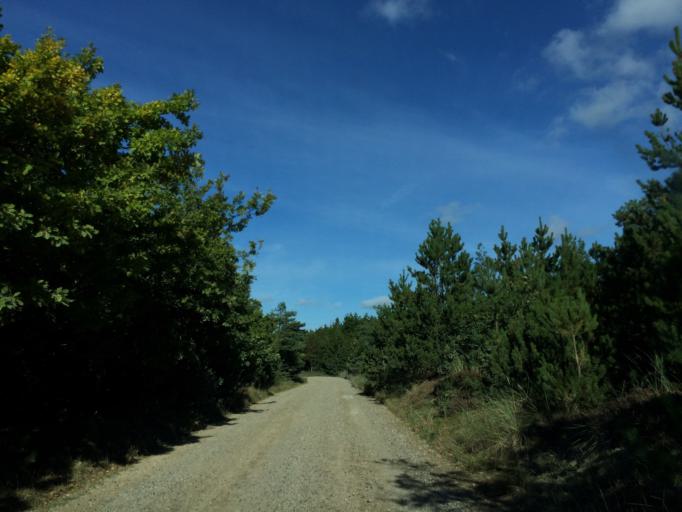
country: DK
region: Central Jutland
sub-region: Holstebro Kommune
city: Ulfborg
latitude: 56.2864
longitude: 8.1472
